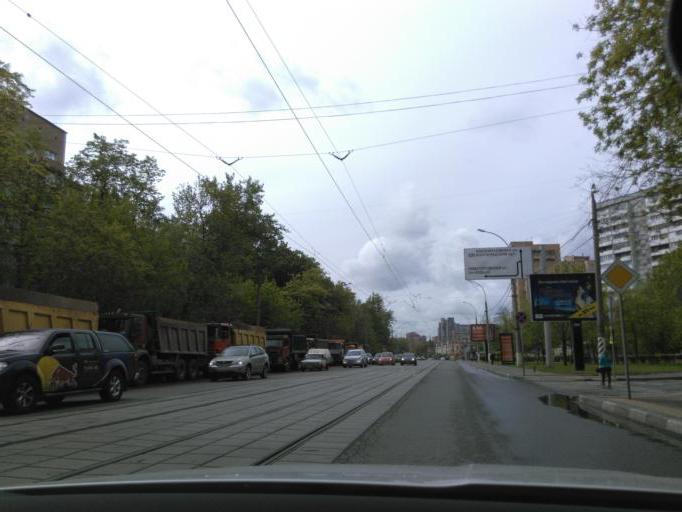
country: RU
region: Moscow
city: Taganskiy
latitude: 55.7419
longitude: 37.6755
